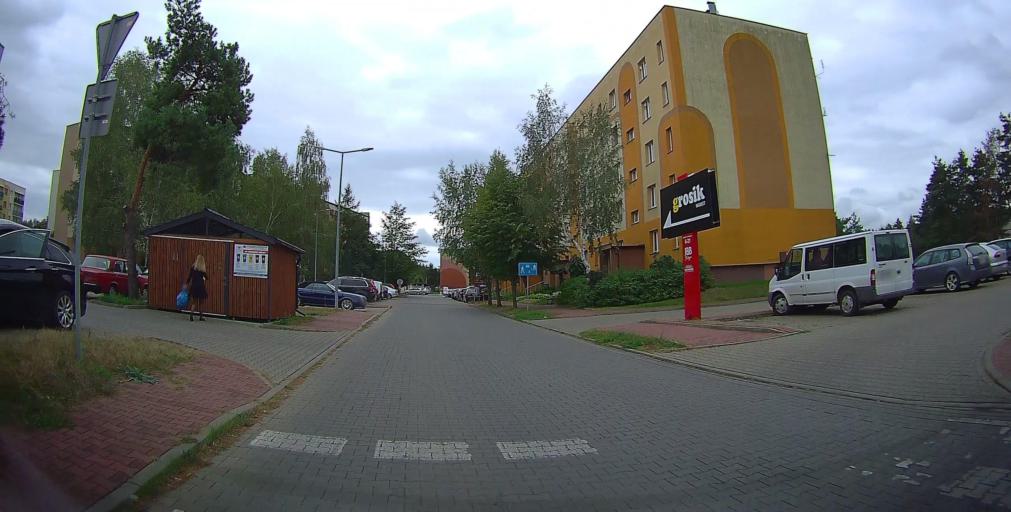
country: PL
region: Masovian Voivodeship
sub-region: Powiat bialobrzeski
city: Bialobrzegi
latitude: 51.6433
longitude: 20.9469
